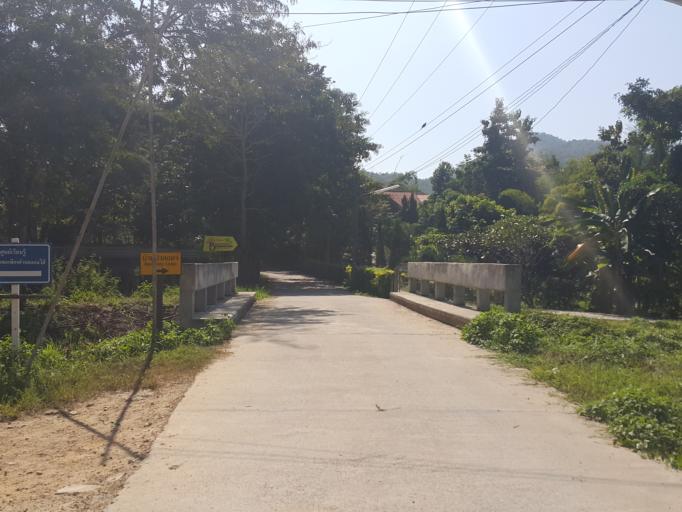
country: TH
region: Chiang Mai
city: Mae On
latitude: 18.7104
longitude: 99.2023
